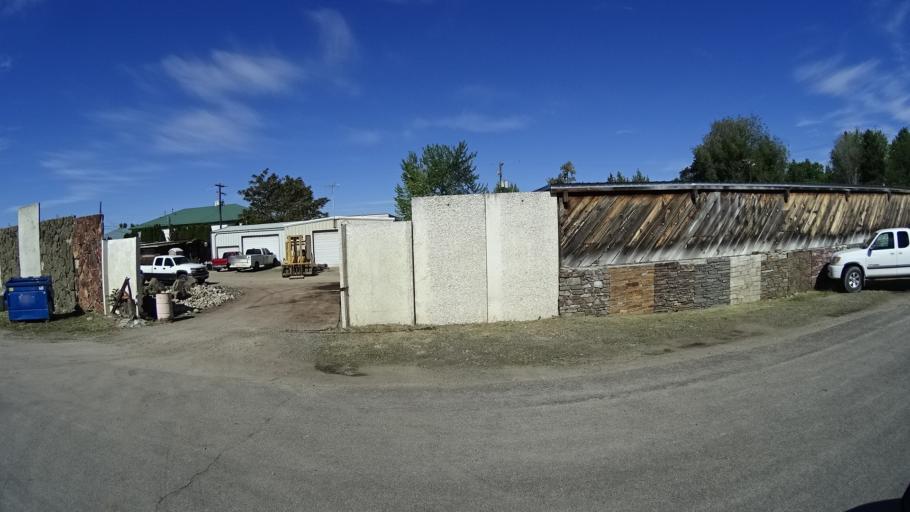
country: US
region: Idaho
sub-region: Ada County
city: Garden City
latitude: 43.6198
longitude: -116.2447
